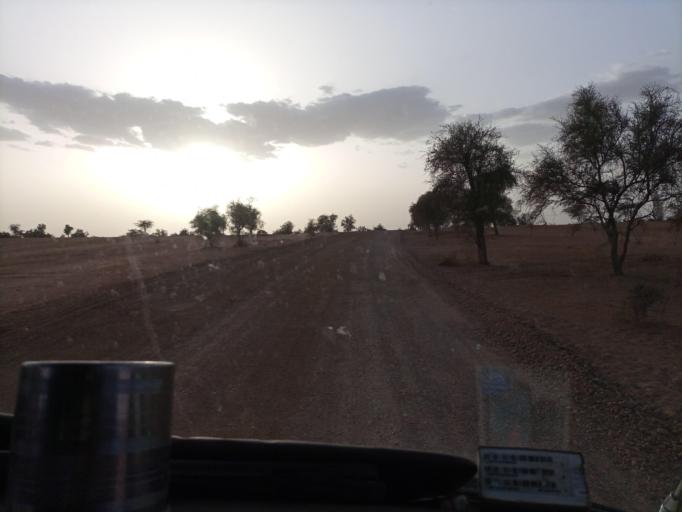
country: SN
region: Louga
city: Dara
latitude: 15.3762
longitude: -15.5910
